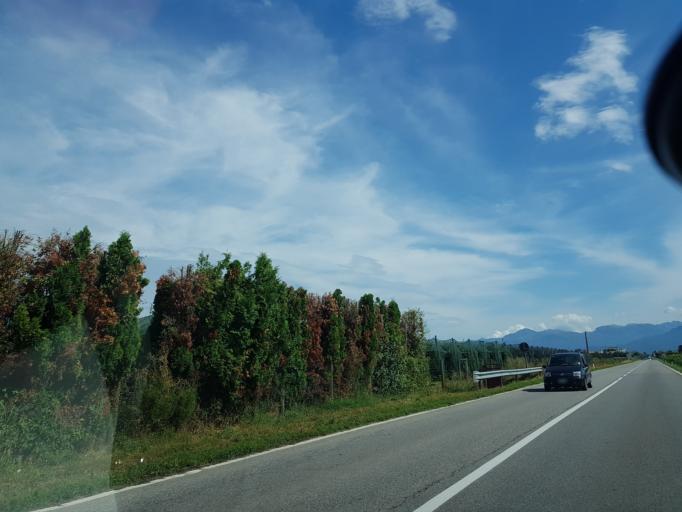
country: IT
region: Piedmont
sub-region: Provincia di Cuneo
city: Roata Rossi
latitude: 44.4377
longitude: 7.5341
